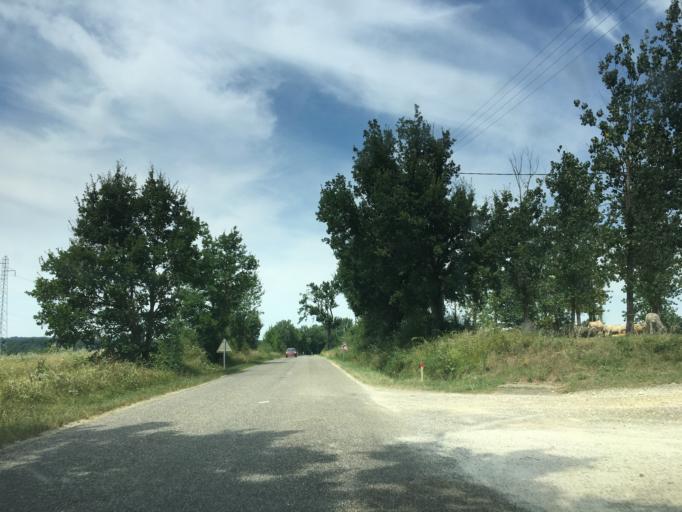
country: FR
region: Midi-Pyrenees
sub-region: Departement du Gers
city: Fleurance
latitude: 43.8264
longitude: 0.6397
